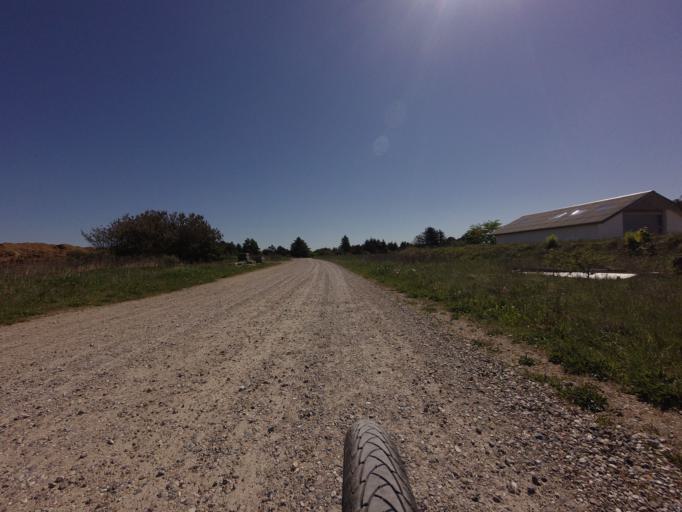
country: DK
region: North Denmark
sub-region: Jammerbugt Kommune
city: Pandrup
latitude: 57.2516
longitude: 9.6226
